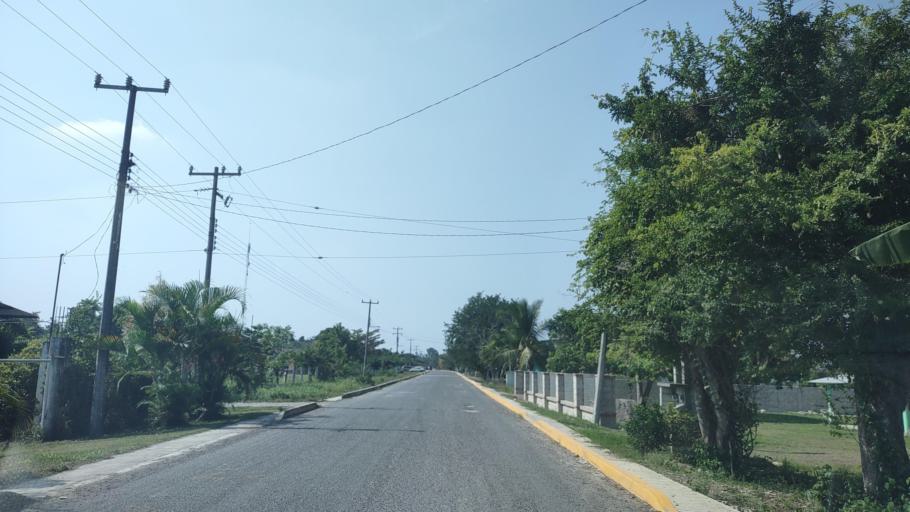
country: MX
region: Puebla
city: Espinal
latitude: 20.2635
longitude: -97.3083
